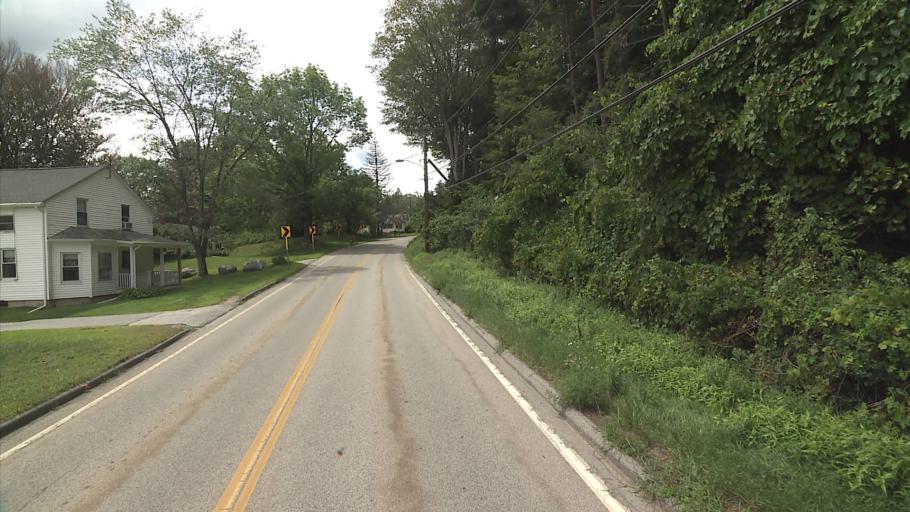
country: US
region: Connecticut
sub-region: Windham County
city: South Woodstock
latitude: 41.9374
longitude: -71.9643
